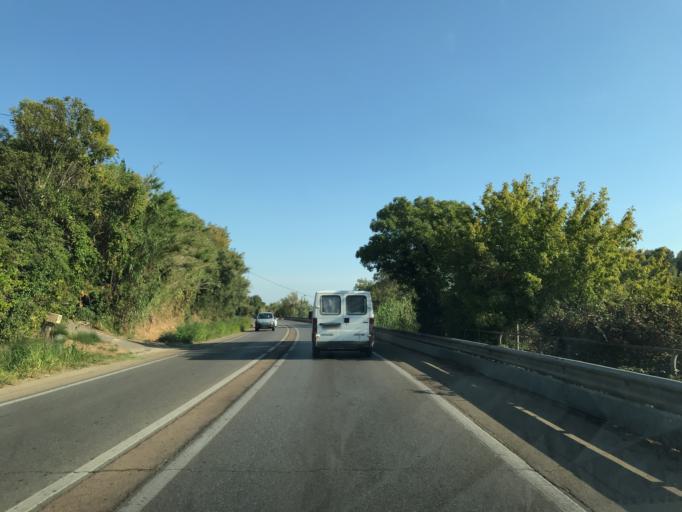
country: FR
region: Provence-Alpes-Cote d'Azur
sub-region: Departement des Bouches-du-Rhone
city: Saint-Chamas
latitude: 43.5559
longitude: 5.0325
